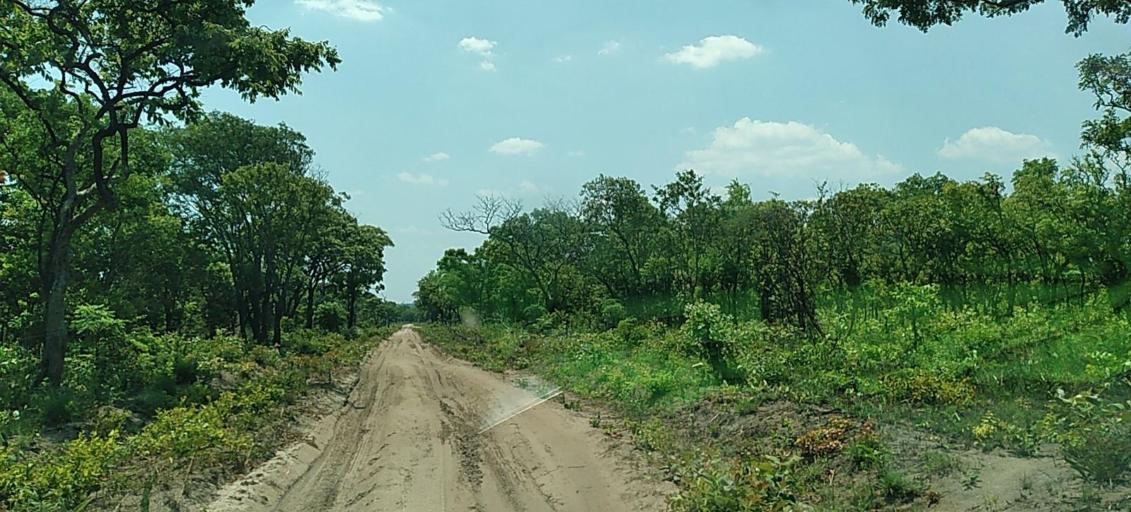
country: CD
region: Katanga
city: Kolwezi
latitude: -11.3015
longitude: 25.2297
